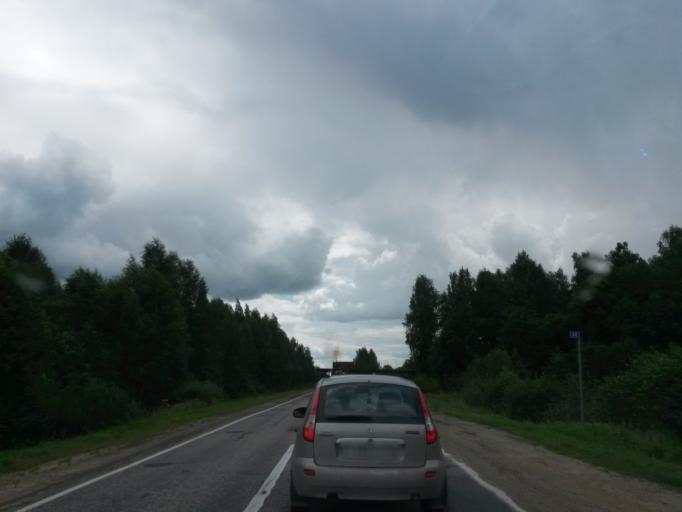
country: RU
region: Jaroslavl
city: Krasnyye Tkachi
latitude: 57.4552
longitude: 39.9113
